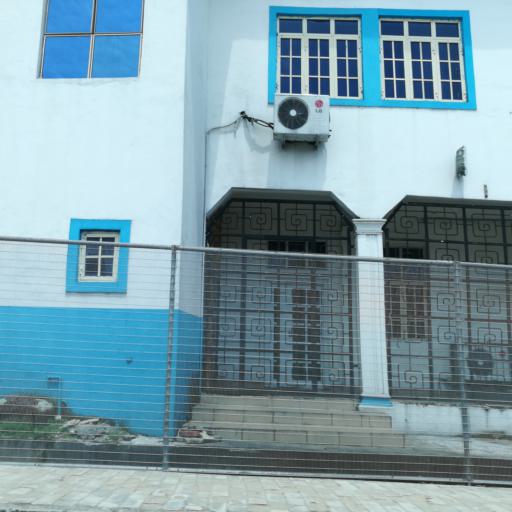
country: NG
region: Rivers
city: Port Harcourt
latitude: 4.7816
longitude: 7.0419
